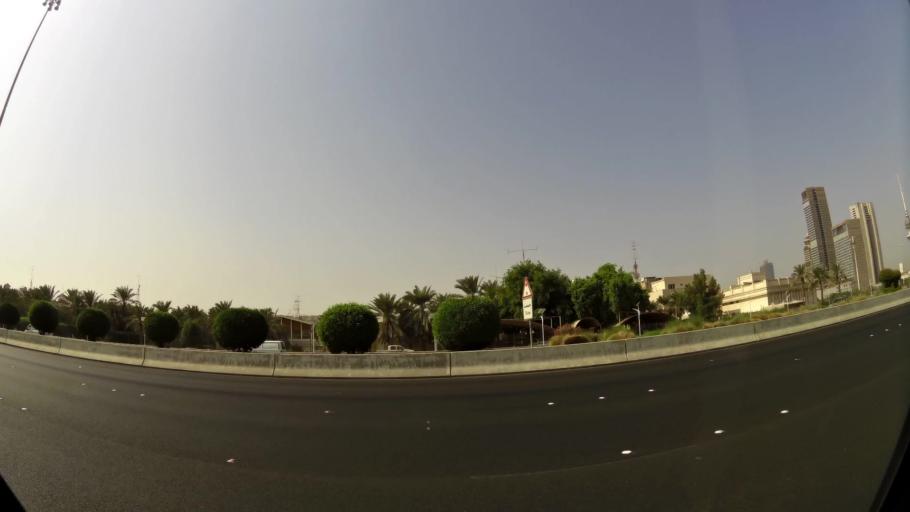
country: KW
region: Al Asimah
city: Ad Dasmah
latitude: 29.3590
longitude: 47.9886
